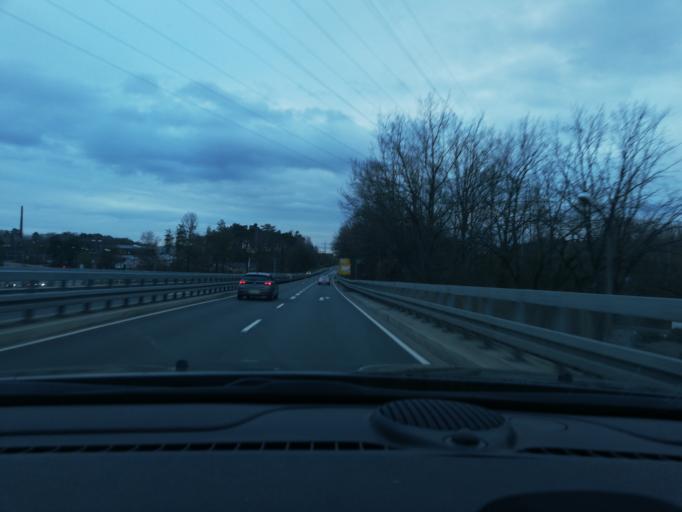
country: DE
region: Bavaria
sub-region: Regierungsbezirk Mittelfranken
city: Erlangen
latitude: 49.5864
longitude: 10.9694
